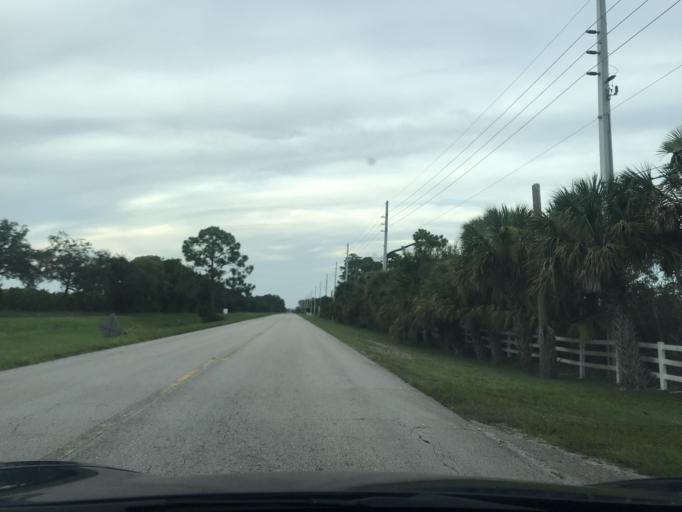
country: US
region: Florida
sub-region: Indian River County
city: West Vero Corridor
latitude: 27.6117
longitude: -80.4961
